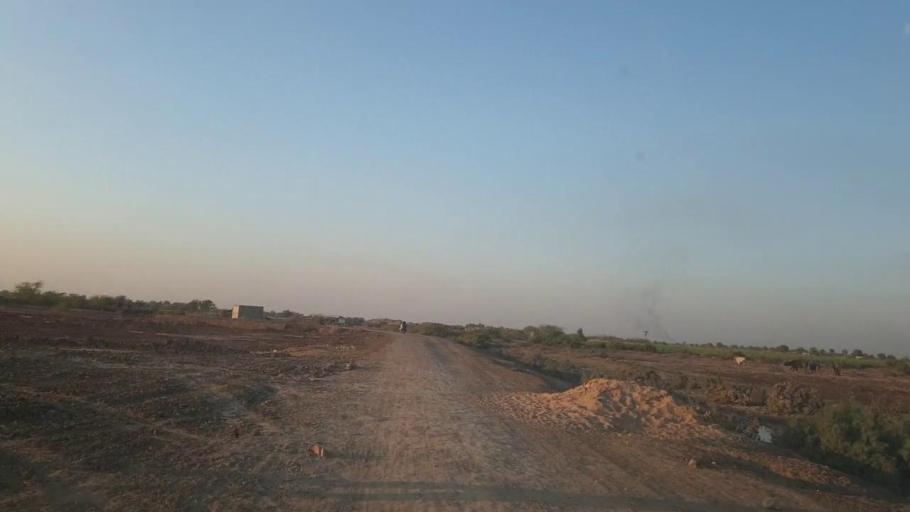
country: PK
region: Sindh
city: Mirpur Khas
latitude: 25.4630
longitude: 69.0716
